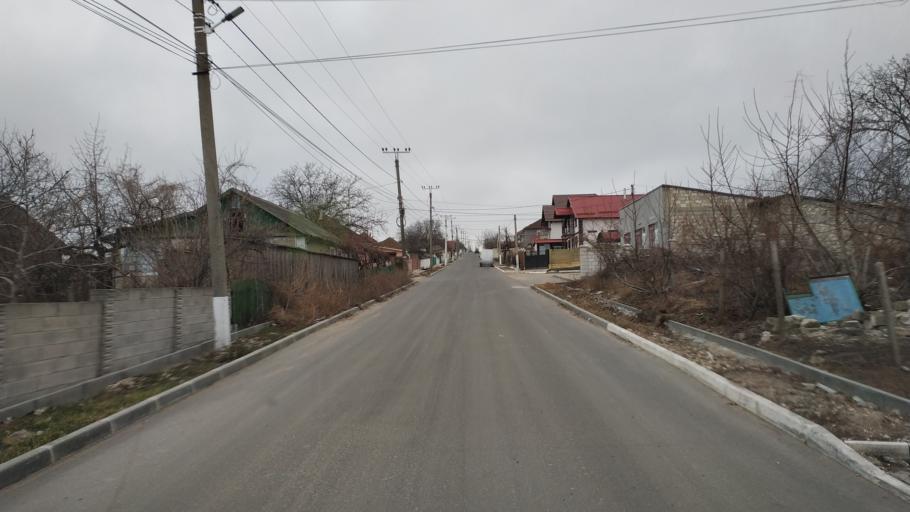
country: MD
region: Laloveni
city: Ialoveni
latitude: 46.9086
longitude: 28.8013
